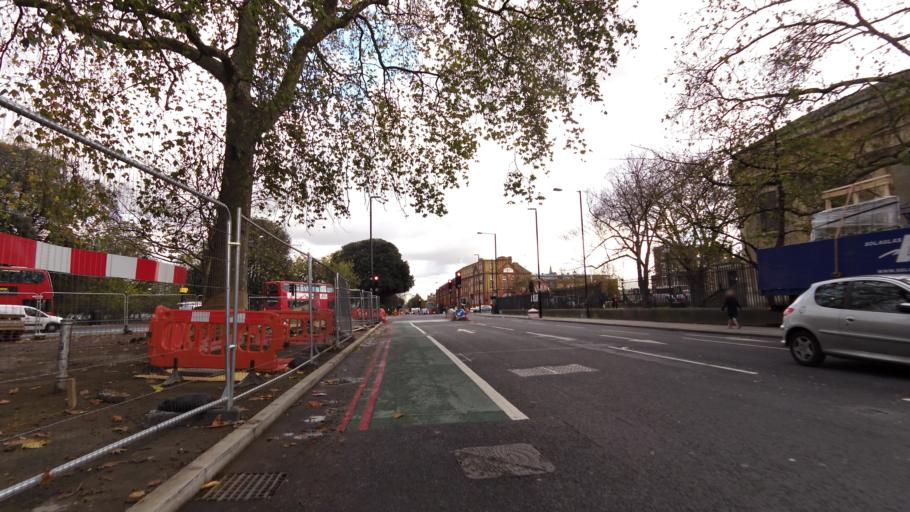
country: GB
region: England
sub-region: Greater London
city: Kennington
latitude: 51.4819
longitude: -0.1119
